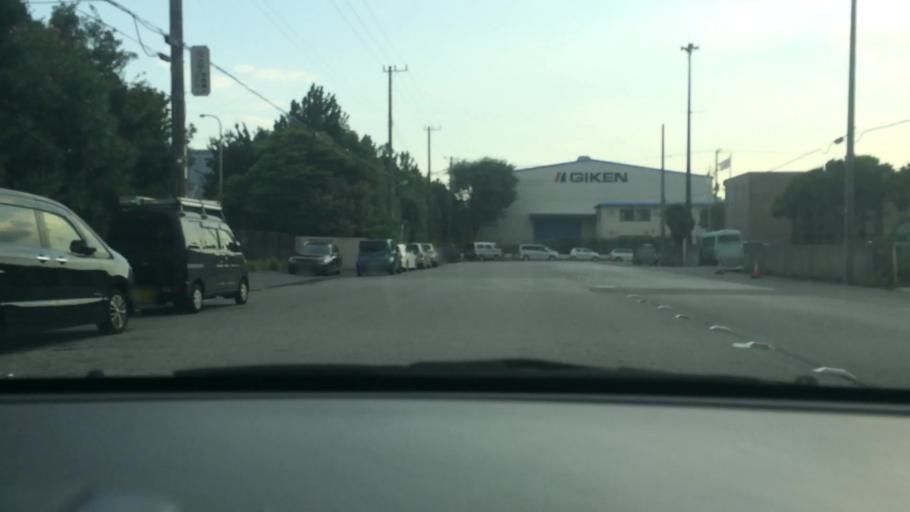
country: JP
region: Tokyo
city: Urayasu
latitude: 35.6299
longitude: 139.9083
